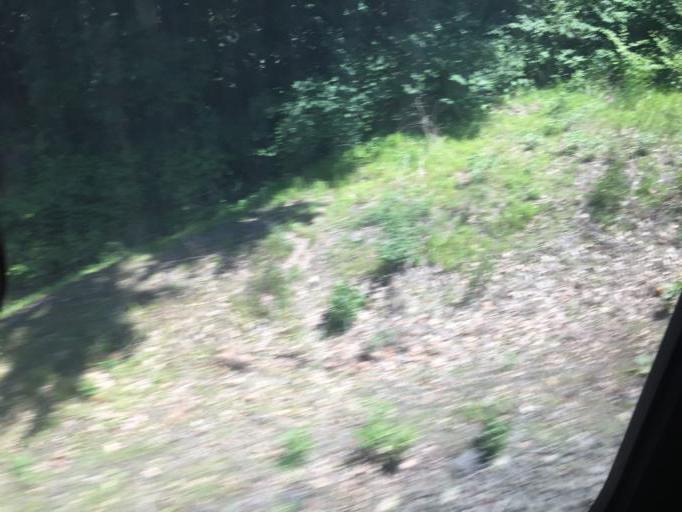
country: US
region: Connecticut
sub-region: New Haven County
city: Wallingford
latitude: 41.4960
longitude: -72.8129
